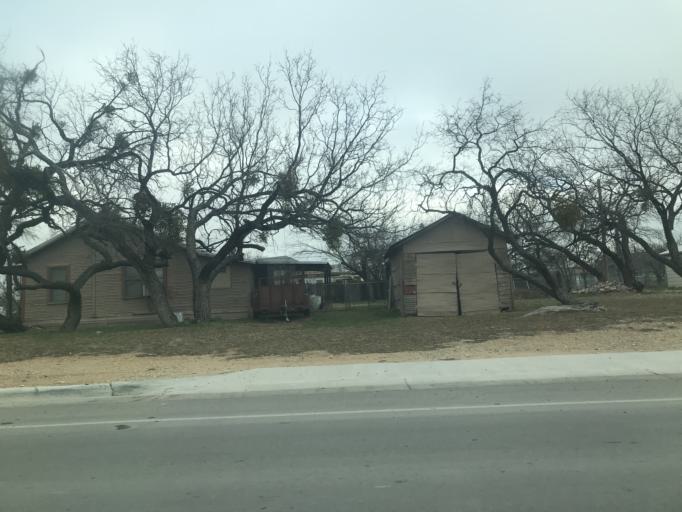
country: US
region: Texas
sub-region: Tom Green County
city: San Angelo
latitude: 31.4841
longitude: -100.4559
